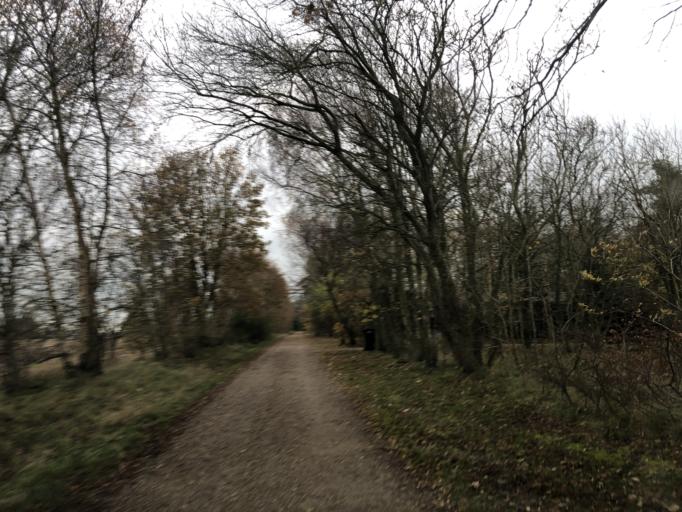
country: DK
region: Central Jutland
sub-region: Holstebro Kommune
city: Ulfborg
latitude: 56.3183
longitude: 8.2171
